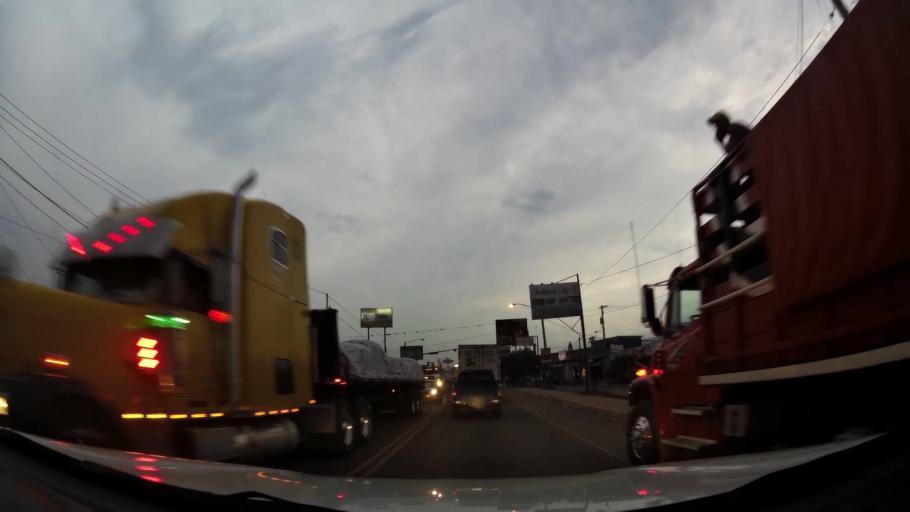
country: NI
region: Esteli
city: Esteli
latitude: 13.0913
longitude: -86.3515
